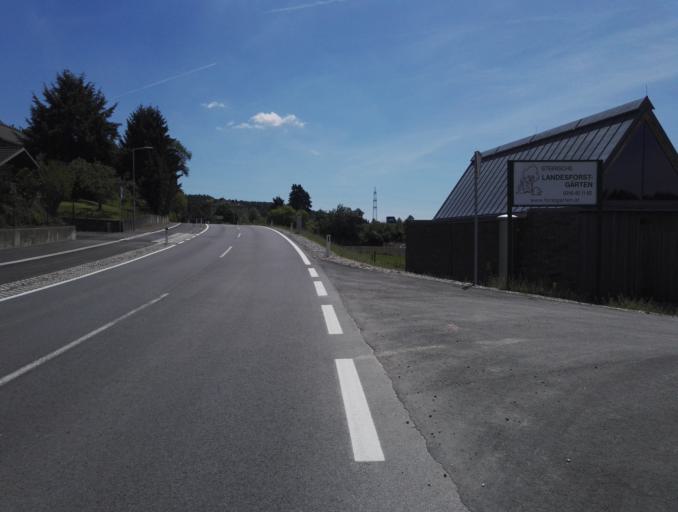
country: AT
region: Styria
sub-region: Politischer Bezirk Graz-Umgebung
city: Grambach
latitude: 47.0228
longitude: 15.4993
